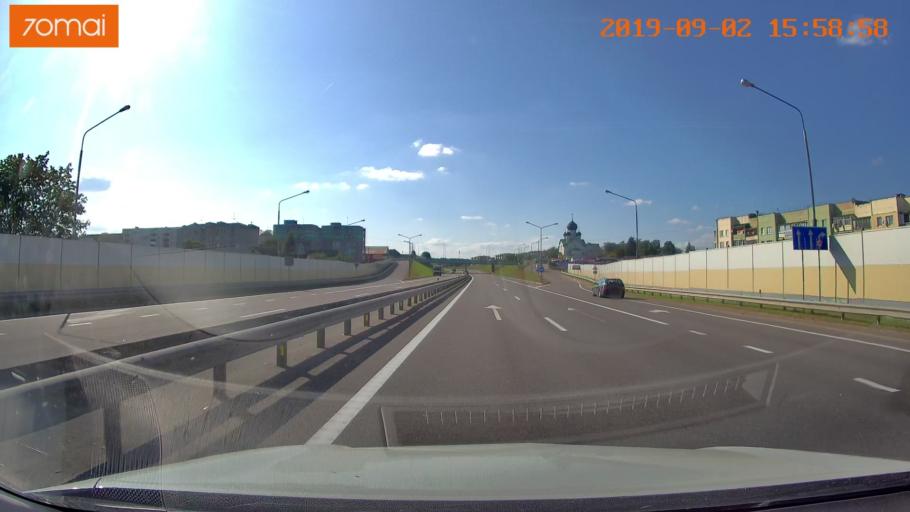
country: BY
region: Minsk
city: Byerazino
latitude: 53.8301
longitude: 28.9974
